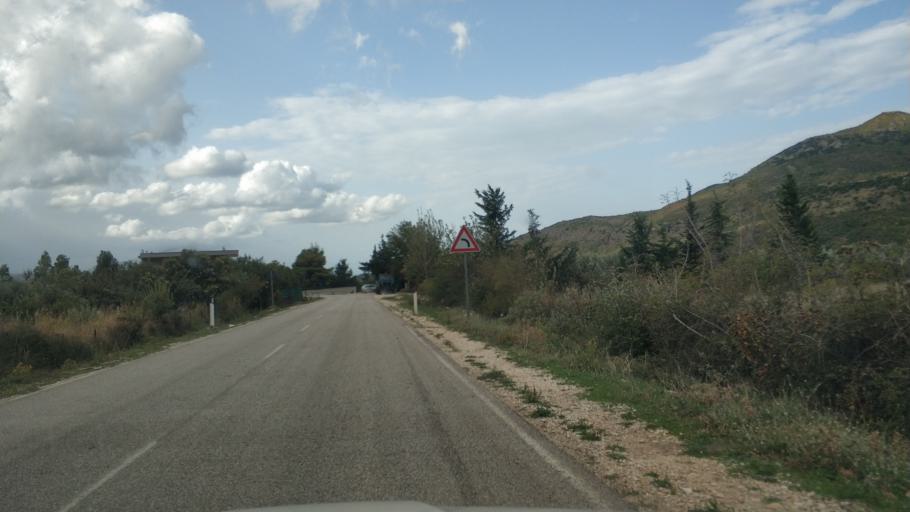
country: AL
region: Vlore
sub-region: Rrethi i Vlores
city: Orikum
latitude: 40.2711
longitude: 19.5130
